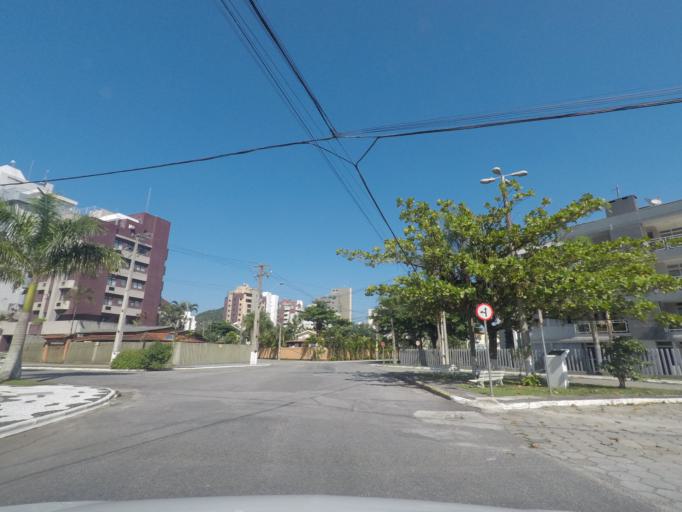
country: BR
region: Parana
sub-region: Guaratuba
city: Guaratuba
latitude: -25.8400
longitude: -48.5408
